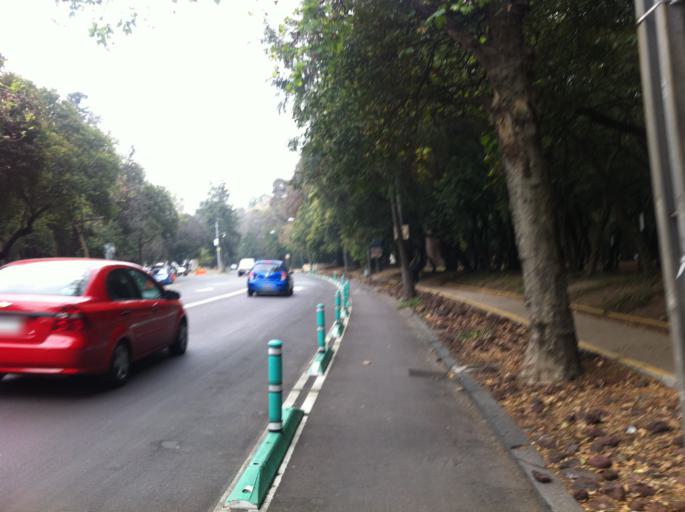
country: MX
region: Mexico City
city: Miguel Hidalgo
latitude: 19.4282
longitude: -99.1831
